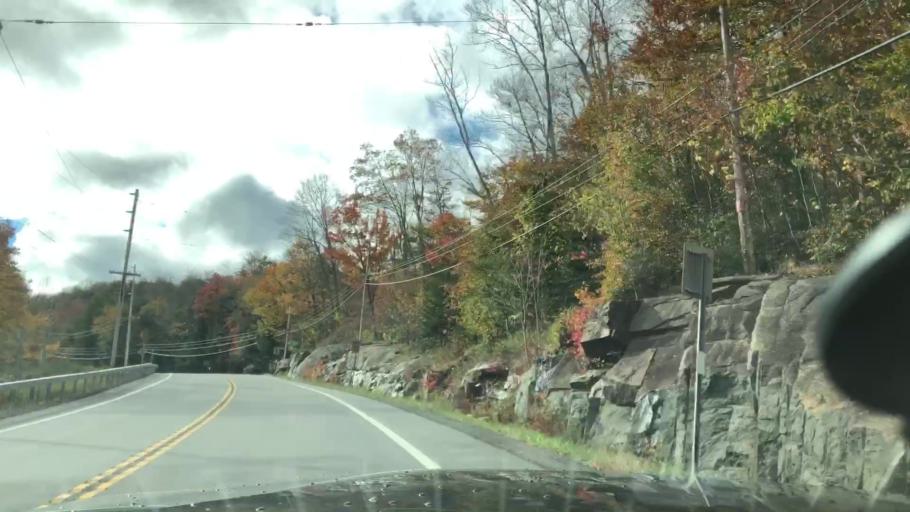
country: US
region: New York
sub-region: Oneida County
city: Boonville
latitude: 43.7331
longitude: -74.9178
